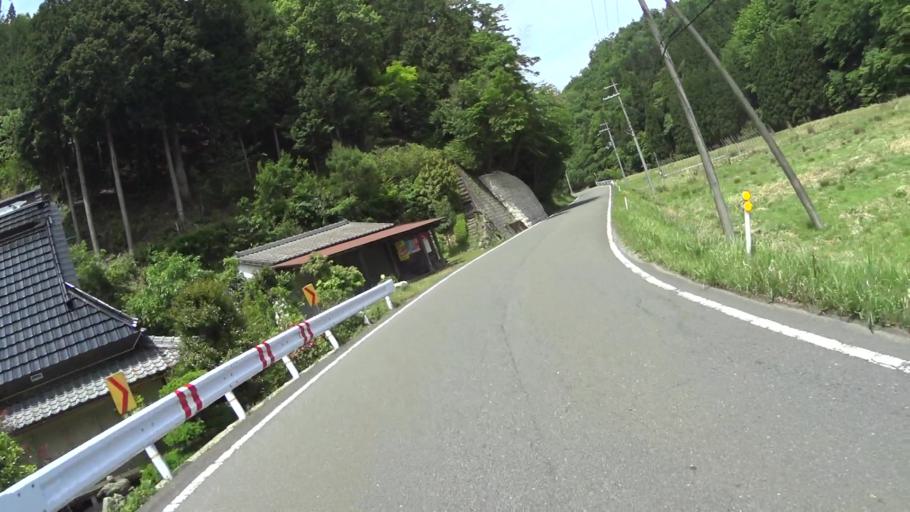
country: JP
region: Kyoto
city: Maizuru
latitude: 35.4143
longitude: 135.4621
